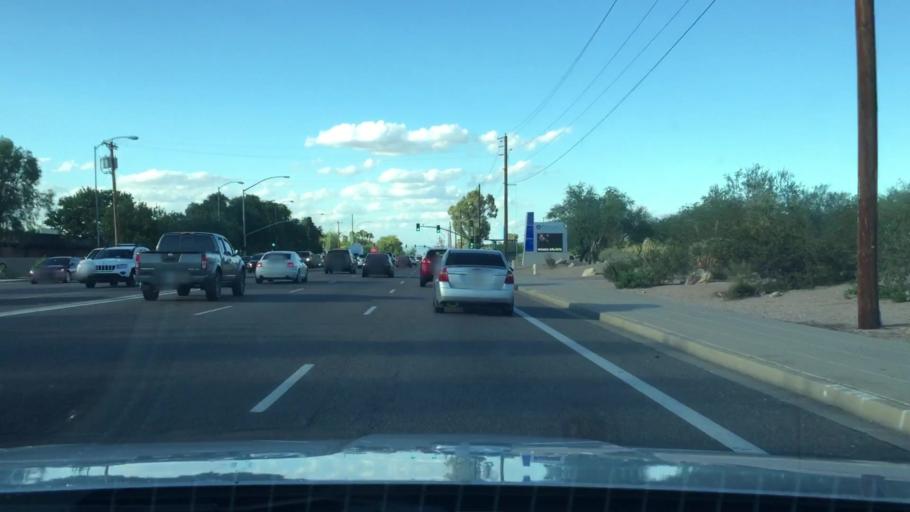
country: US
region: Arizona
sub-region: Maricopa County
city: Tempe
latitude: 33.3900
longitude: -111.8745
